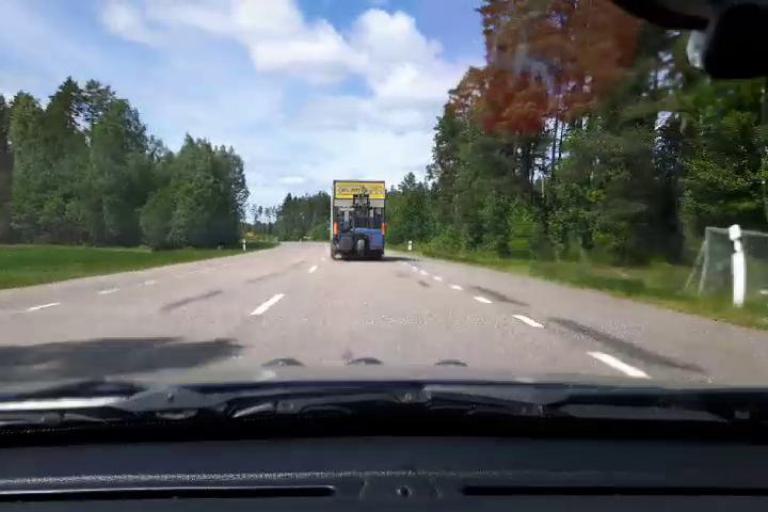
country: SE
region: Uppsala
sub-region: Osthammars Kommun
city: Bjorklinge
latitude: 60.1052
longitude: 17.5478
